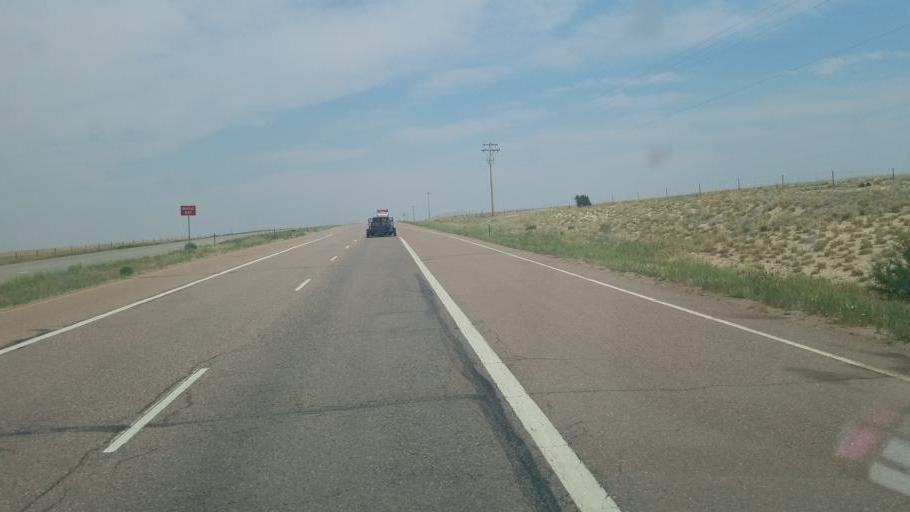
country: US
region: Colorado
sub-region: Fremont County
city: Penrose
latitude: 38.3710
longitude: -104.9355
